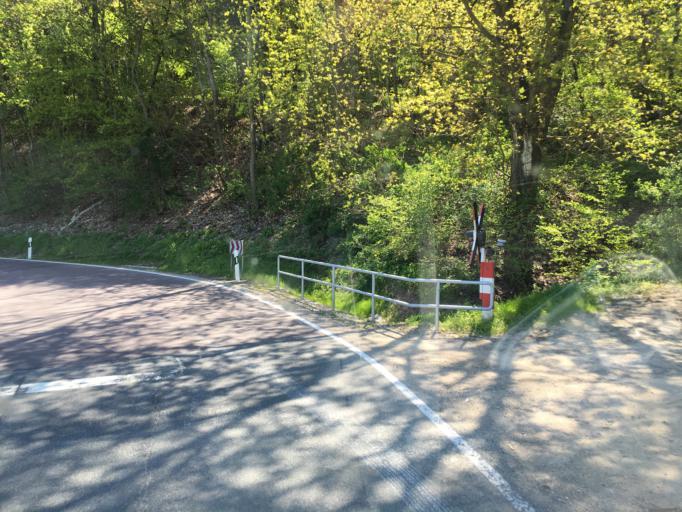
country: DE
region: Saxony-Anhalt
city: Laucha
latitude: 51.2148
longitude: 11.7027
